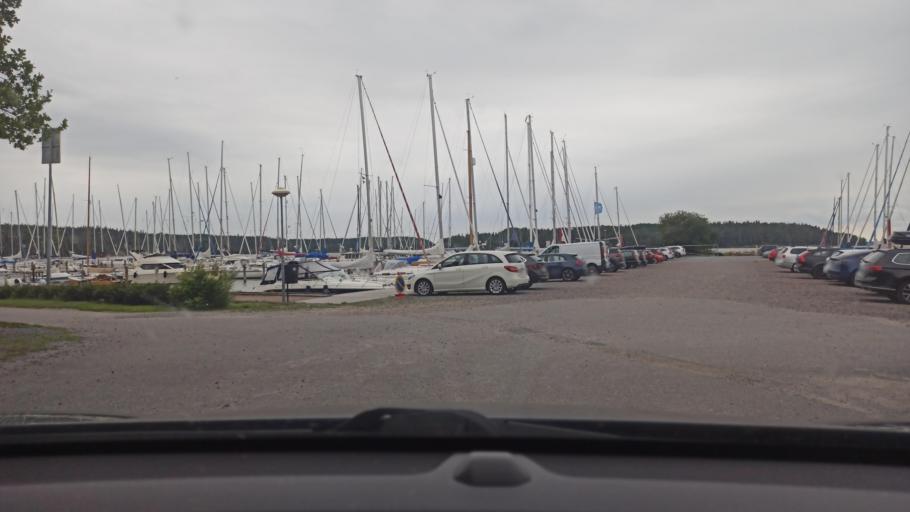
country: FI
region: Varsinais-Suomi
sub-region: Turku
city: Raisio
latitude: 60.4265
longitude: 22.1587
